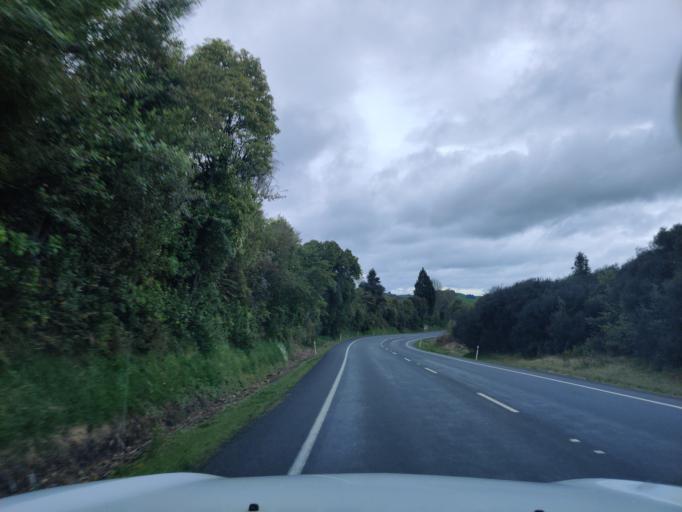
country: NZ
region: Waikato
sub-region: Otorohanga District
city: Otorohanga
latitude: -38.5071
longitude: 175.2046
